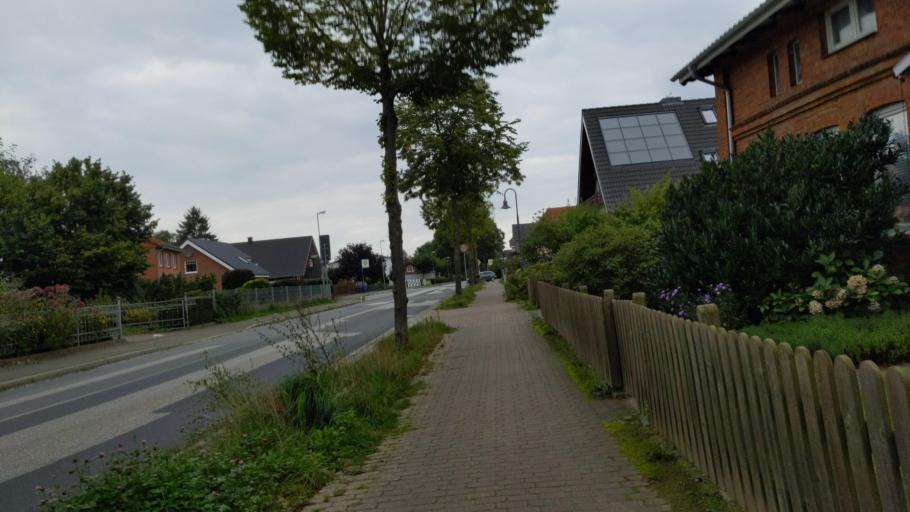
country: DE
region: Schleswig-Holstein
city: Krummesse
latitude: 53.7831
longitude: 10.6409
